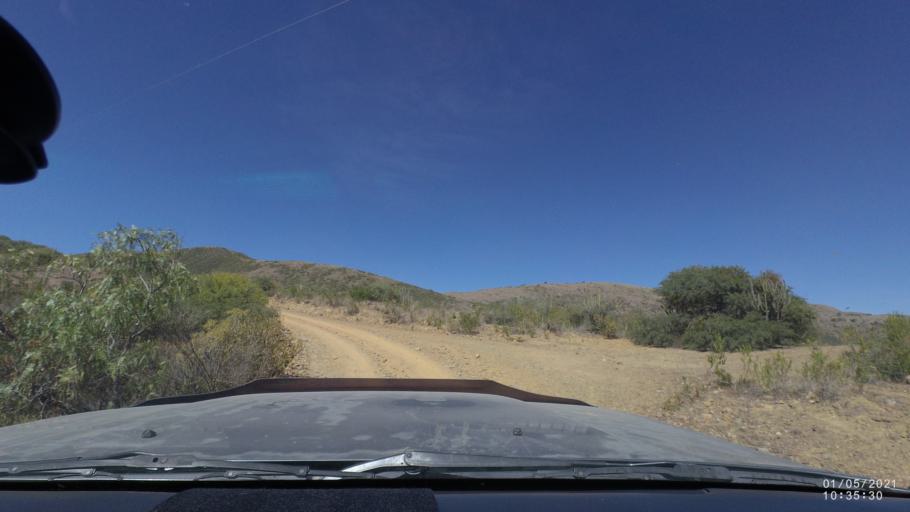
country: BO
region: Cochabamba
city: Capinota
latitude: -17.5981
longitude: -66.1896
